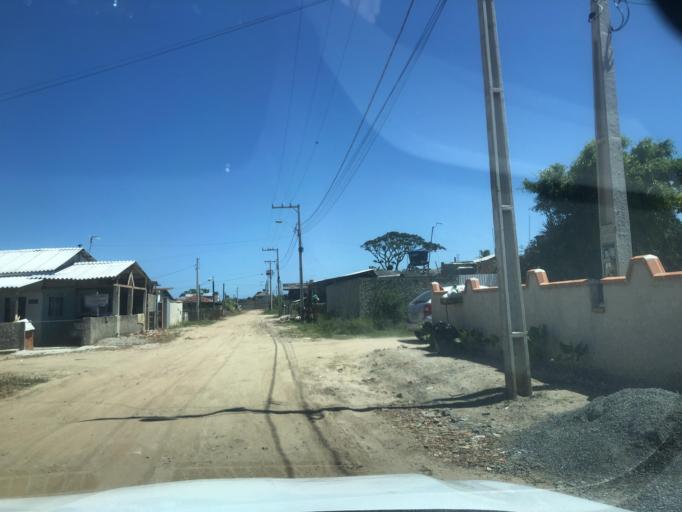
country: BR
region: Santa Catarina
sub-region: Sao Francisco Do Sul
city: Sao Francisco do Sul
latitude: -26.2298
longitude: -48.5225
